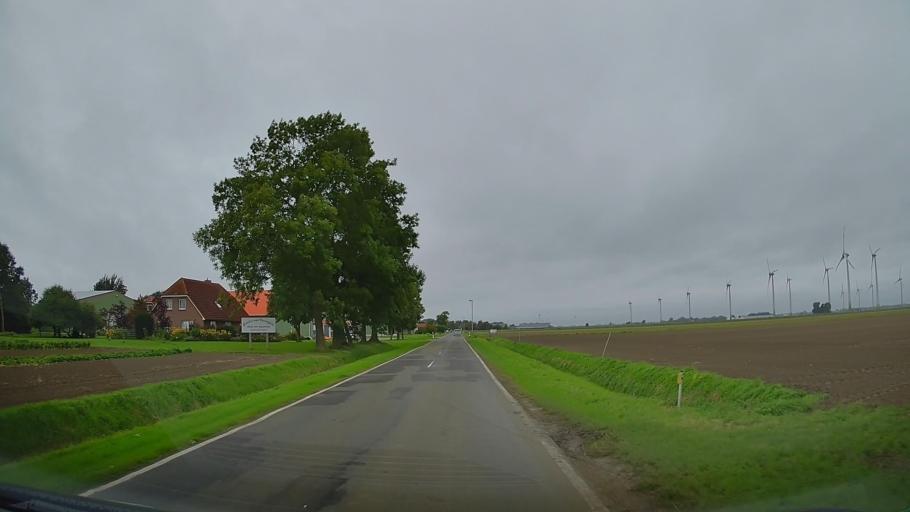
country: DE
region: Schleswig-Holstein
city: Neufeld
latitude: 53.9120
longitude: 9.0040
